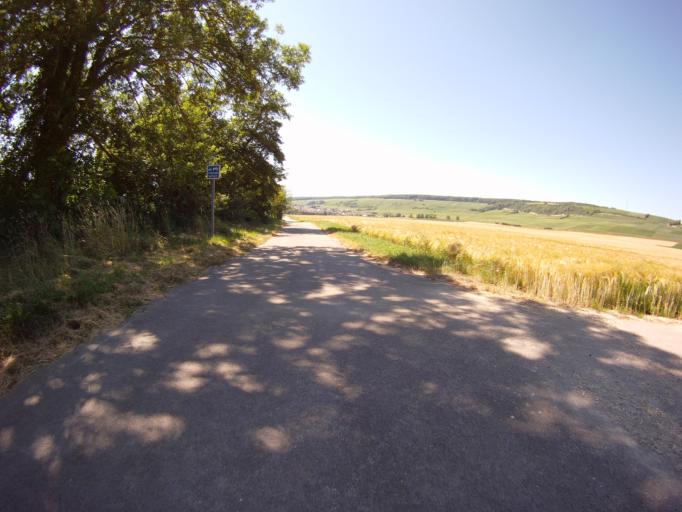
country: FR
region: Champagne-Ardenne
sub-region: Departement de la Marne
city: Dormans
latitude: 49.0890
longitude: 3.6651
